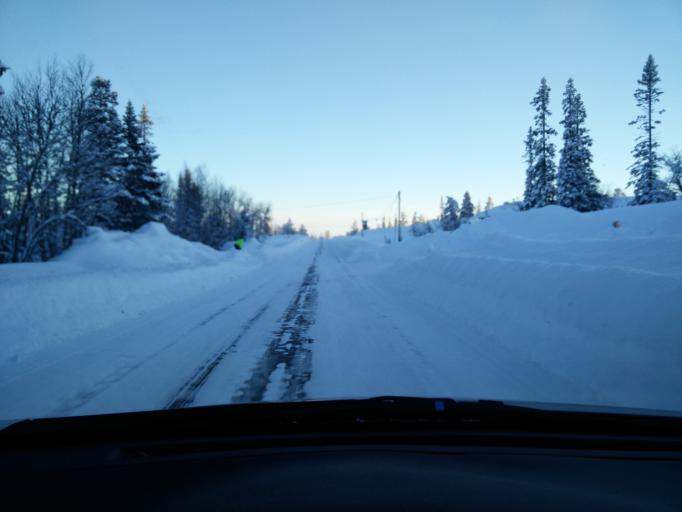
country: SE
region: Jaemtland
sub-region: Bergs Kommun
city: Hoverberg
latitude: 62.4959
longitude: 14.1126
